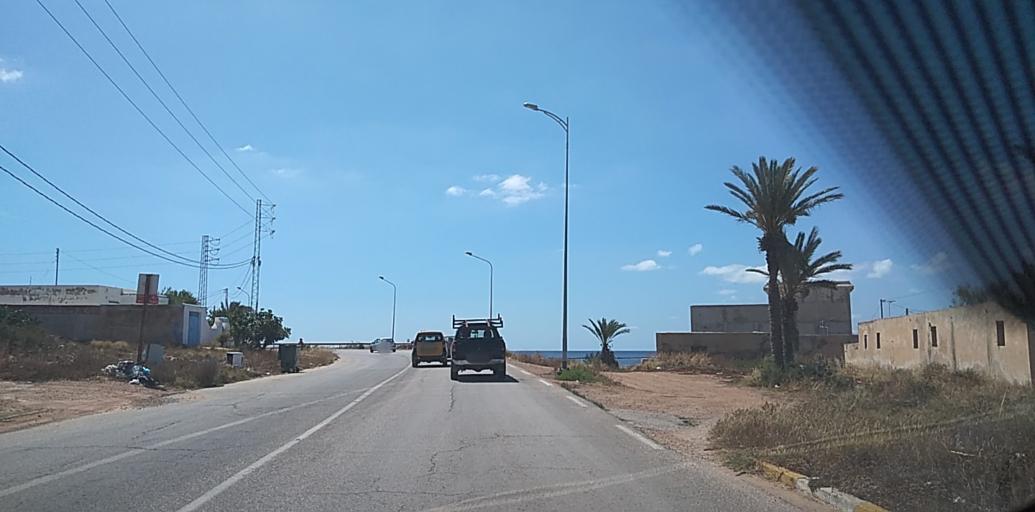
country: TN
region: Safaqis
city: Al Qarmadah
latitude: 34.6728
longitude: 11.1417
